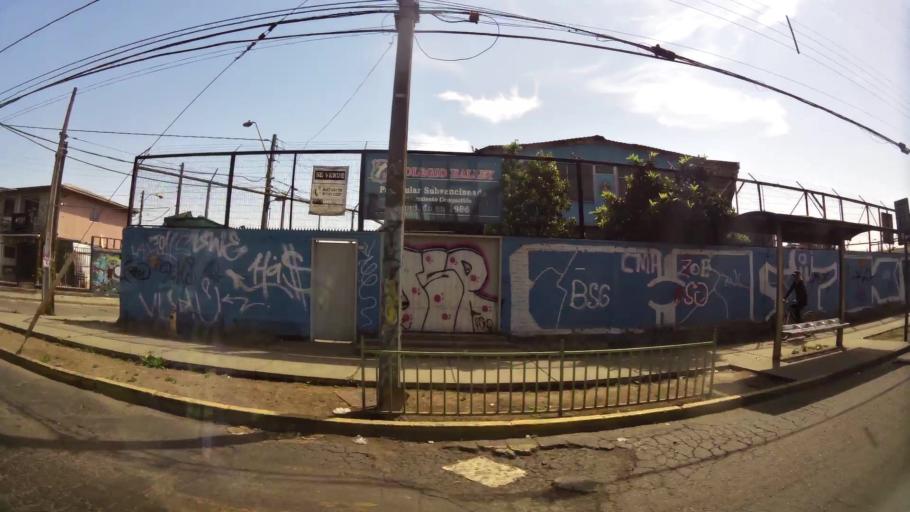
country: CL
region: Santiago Metropolitan
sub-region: Provincia de Santiago
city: Lo Prado
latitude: -33.4781
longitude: -70.7295
